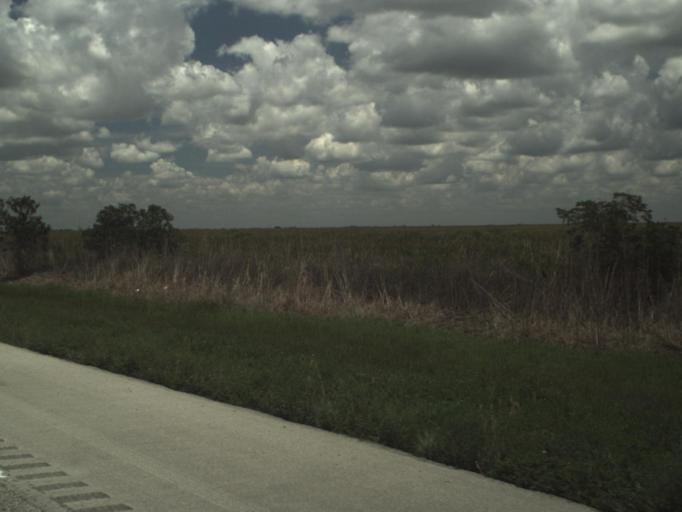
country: US
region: Florida
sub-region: Broward County
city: Weston
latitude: 26.1465
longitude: -80.6042
